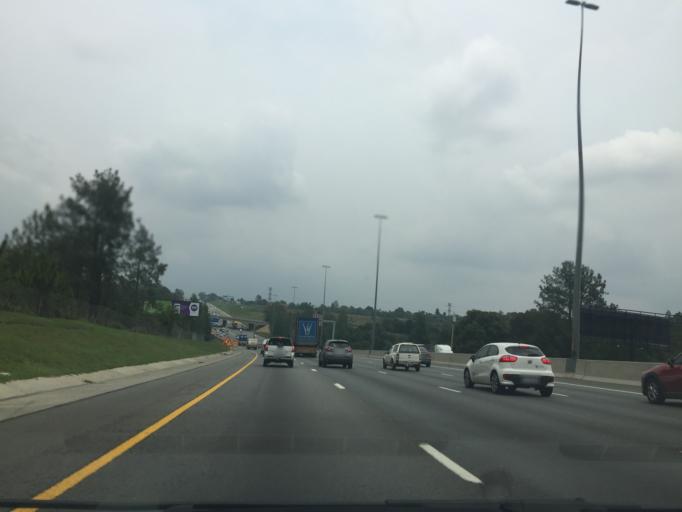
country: ZA
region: Gauteng
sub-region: City of Johannesburg Metropolitan Municipality
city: Diepsloot
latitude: -26.0341
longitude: 28.0315
